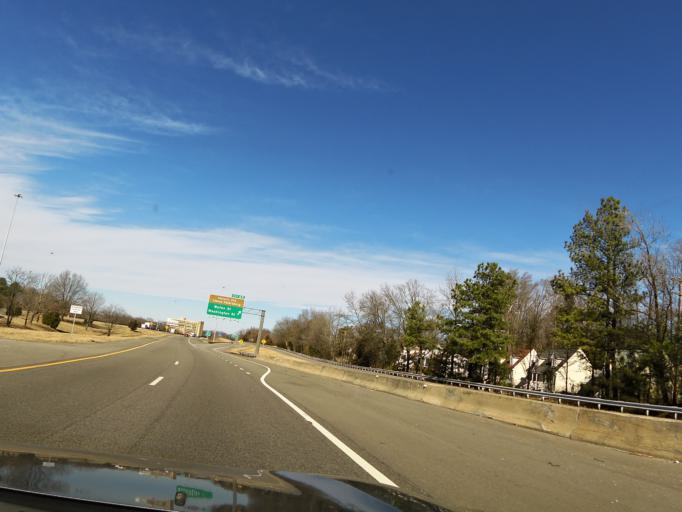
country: US
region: Virginia
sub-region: City of Petersburg
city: Petersburg
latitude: 37.2223
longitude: -77.3902
